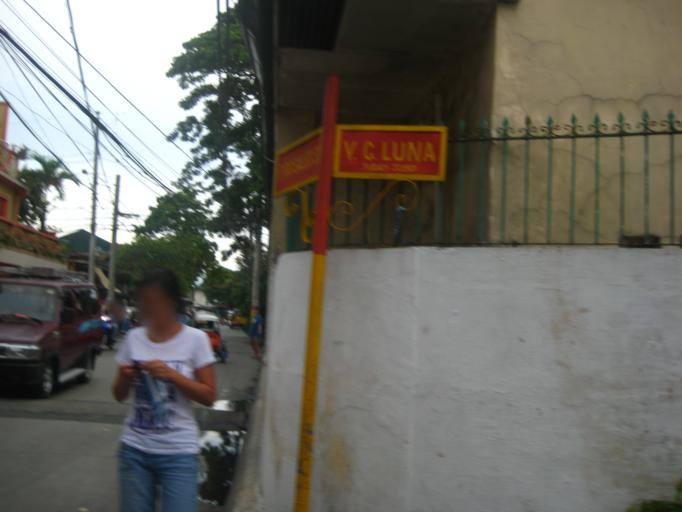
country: PH
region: Calabarzon
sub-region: Province of Rizal
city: Pateros
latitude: 14.5474
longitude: 121.0742
